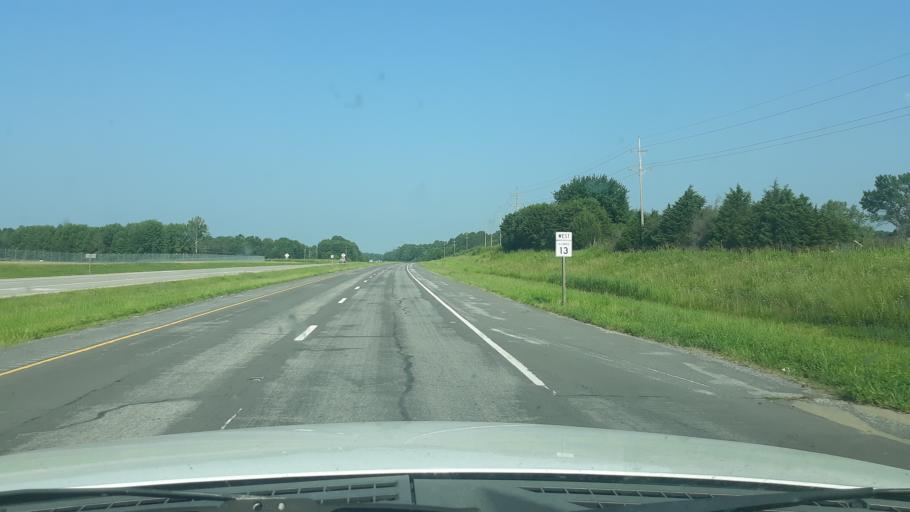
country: US
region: Illinois
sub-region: Saline County
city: Carrier Mills
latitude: 37.7336
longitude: -88.6735
